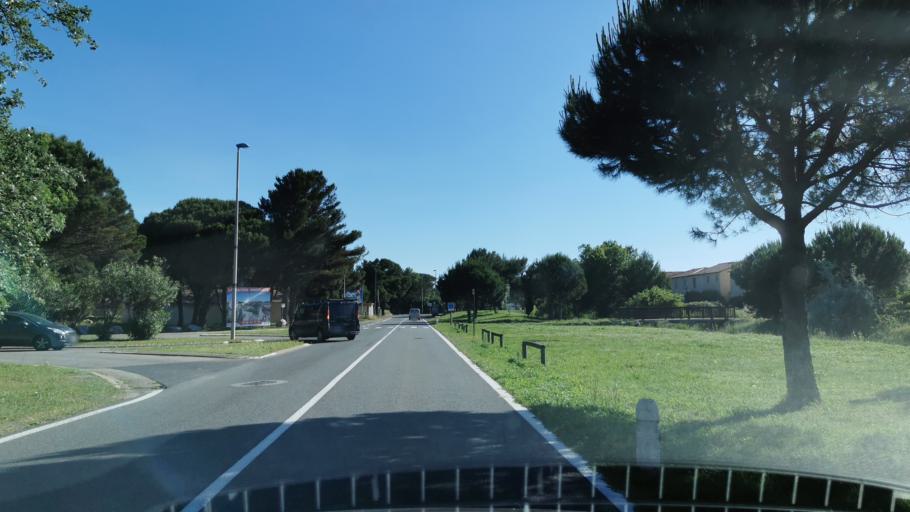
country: FR
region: Languedoc-Roussillon
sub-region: Departement de l'Aude
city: Armissan
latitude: 43.1586
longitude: 3.1602
